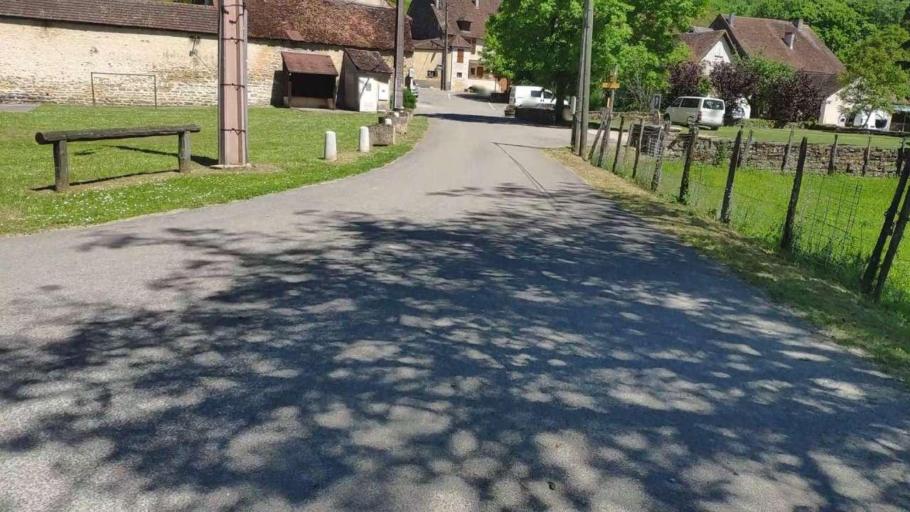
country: FR
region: Franche-Comte
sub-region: Departement du Jura
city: Perrigny
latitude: 46.7438
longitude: 5.6262
